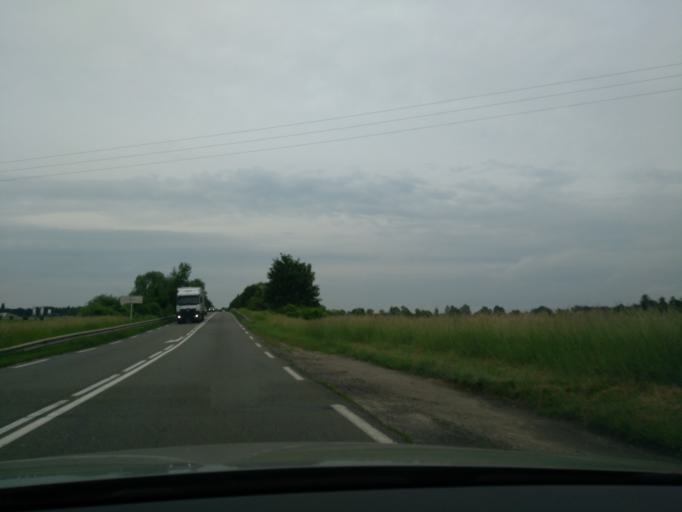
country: FR
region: Picardie
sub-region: Departement de l'Aisne
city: Athies-sous-Laon
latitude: 49.5996
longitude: 3.6614
